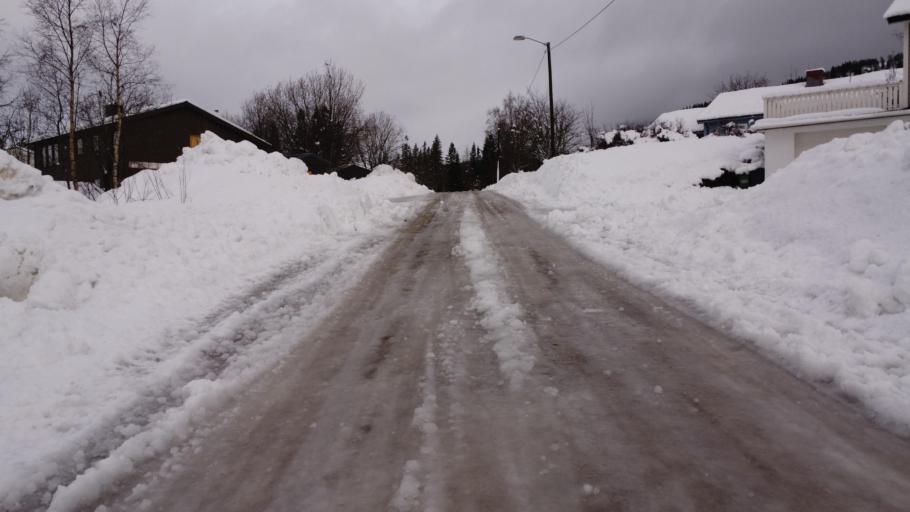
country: NO
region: Nordland
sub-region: Rana
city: Mo i Rana
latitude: 66.3332
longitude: 14.1505
